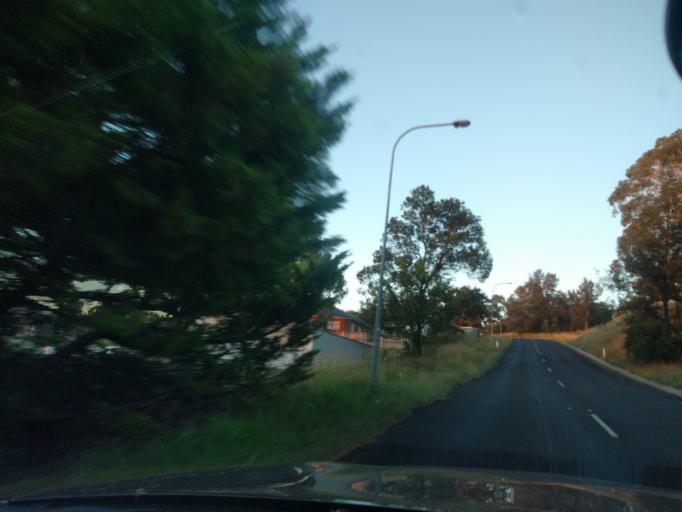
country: AU
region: New South Wales
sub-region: Armidale Dumaresq
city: Armidale
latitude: -30.5020
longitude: 151.6615
